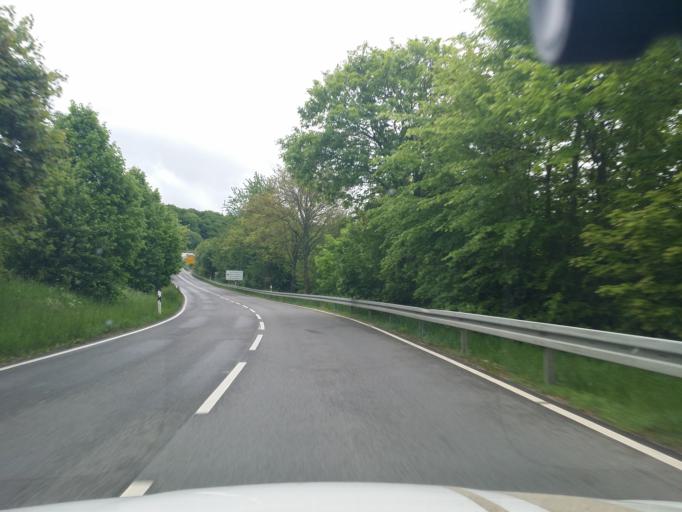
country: DE
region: Hesse
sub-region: Regierungsbezirk Darmstadt
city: Idstein
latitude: 50.1874
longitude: 8.2919
